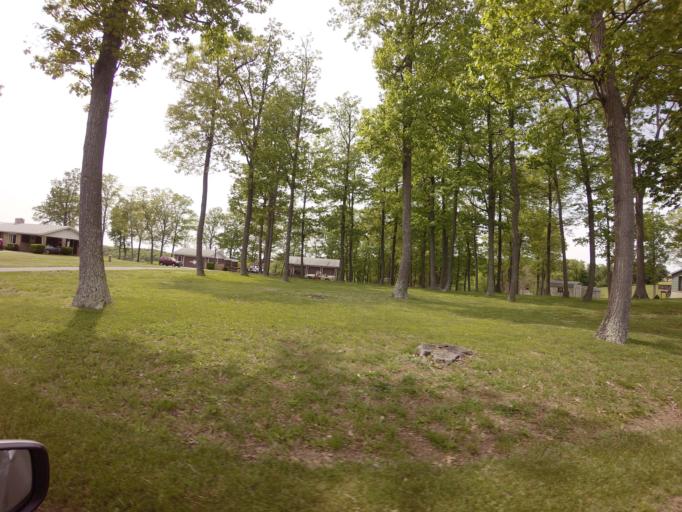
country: US
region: Maryland
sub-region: Carroll County
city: Eldersburg
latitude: 39.4801
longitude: -76.9753
